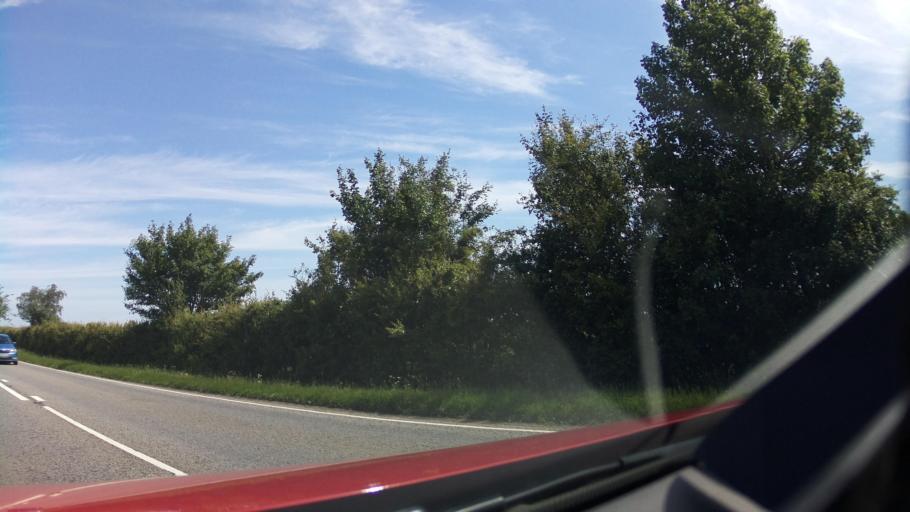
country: GB
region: England
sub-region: North Lincolnshire
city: Kirton in Lindsey
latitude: 53.3791
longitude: -0.5467
